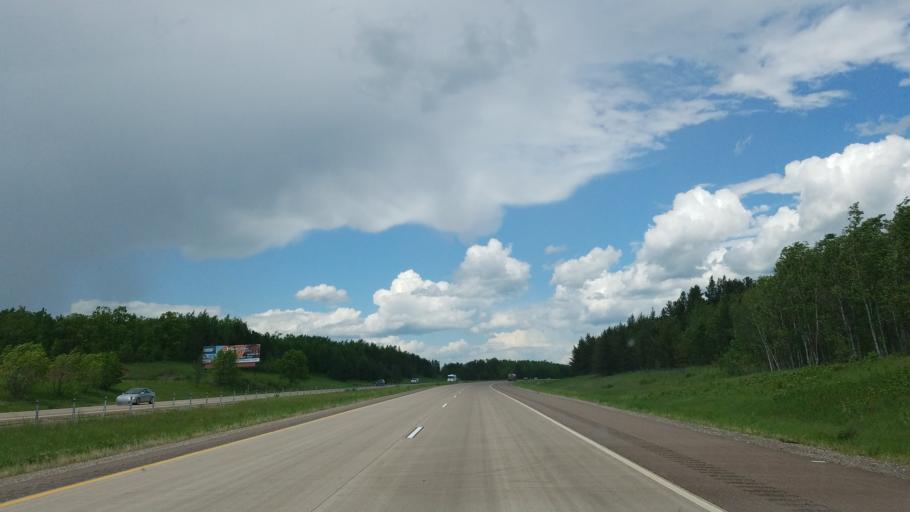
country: US
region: Minnesota
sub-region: Carlton County
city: Moose Lake
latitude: 46.4824
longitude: -92.7091
